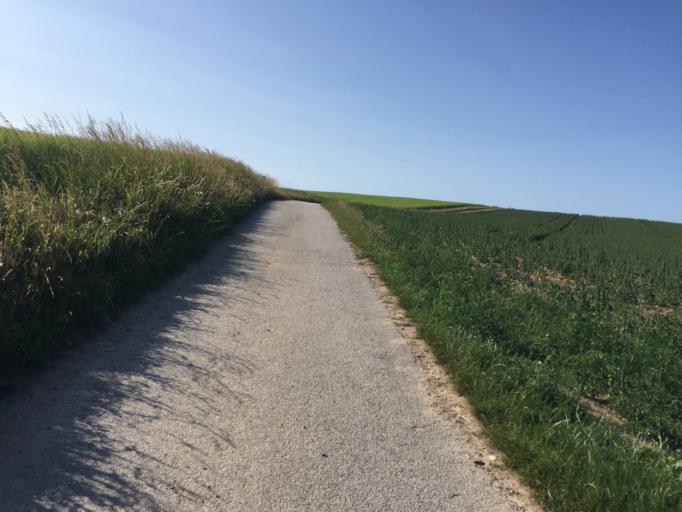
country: DK
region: Zealand
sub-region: Slagelse Kommune
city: Skaelskor
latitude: 55.2023
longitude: 11.1939
